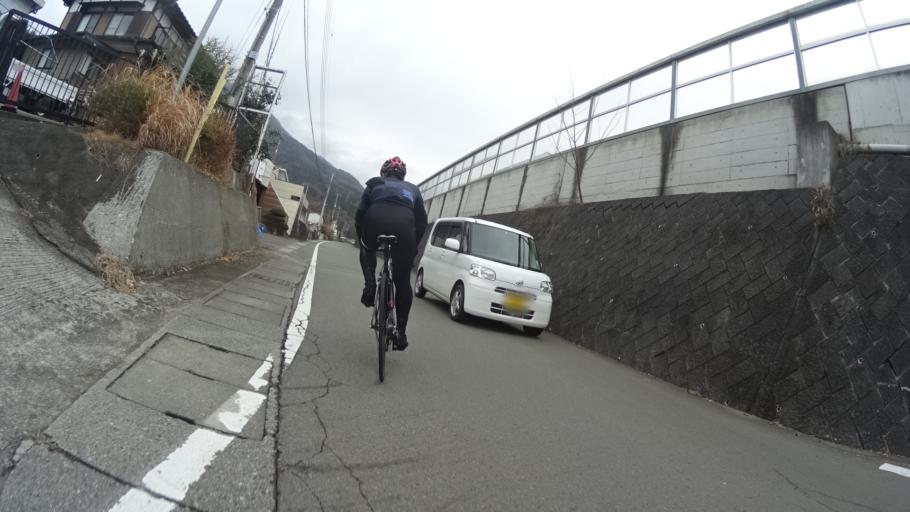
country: JP
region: Yamanashi
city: Otsuki
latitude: 35.6202
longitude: 138.9856
